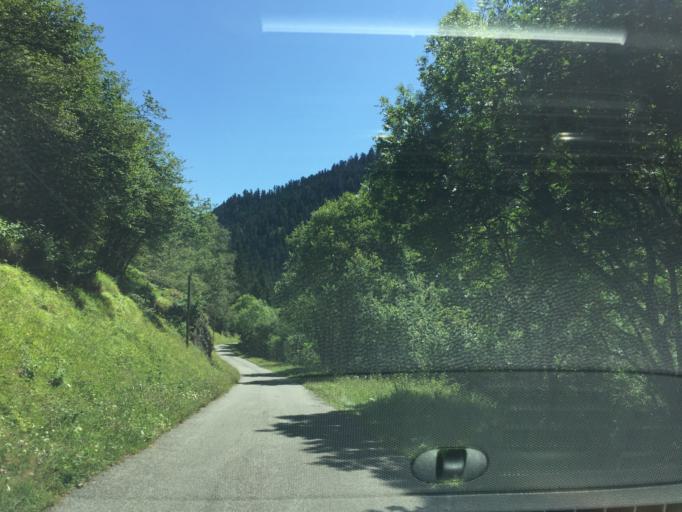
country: FR
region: Midi-Pyrenees
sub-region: Departement des Hautes-Pyrenees
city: Saint-Lary-Soulan
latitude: 42.8491
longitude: 0.2779
